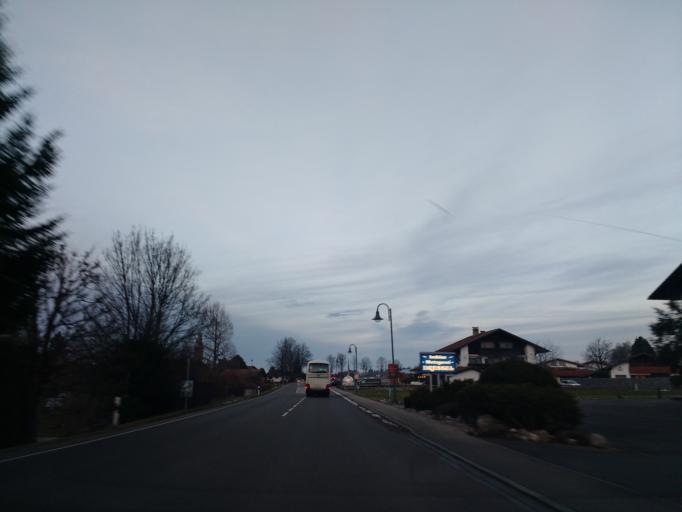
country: DE
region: Bavaria
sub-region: Swabia
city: Halblech
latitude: 47.6187
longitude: 10.8085
